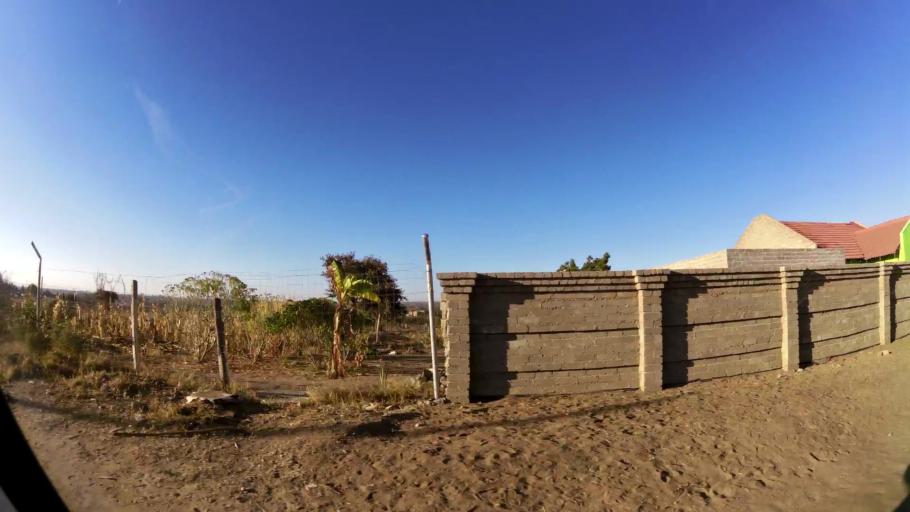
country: ZA
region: Limpopo
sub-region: Capricorn District Municipality
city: Polokwane
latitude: -23.8392
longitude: 29.3570
